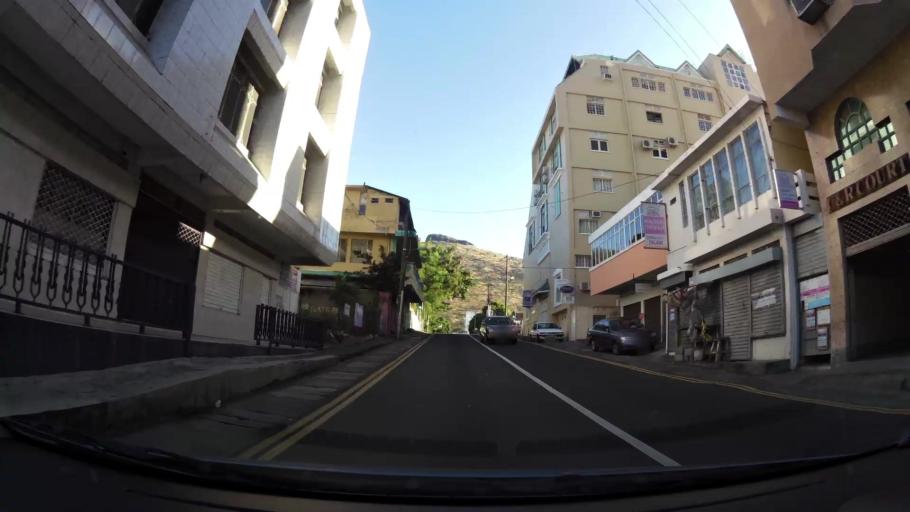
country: MU
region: Port Louis
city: Port Louis
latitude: -20.1692
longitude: 57.5048
